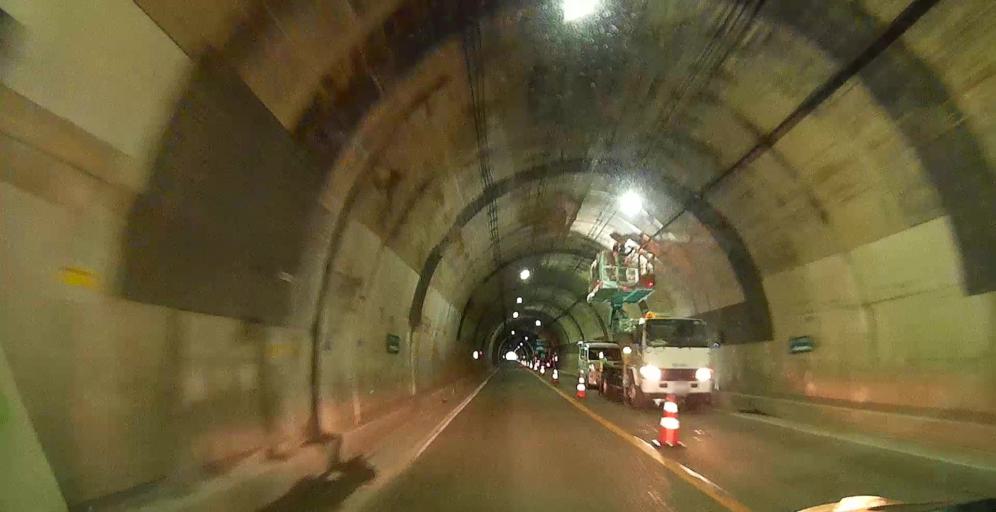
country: JP
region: Kumamoto
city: Yatsushiro
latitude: 32.3712
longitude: 130.5295
